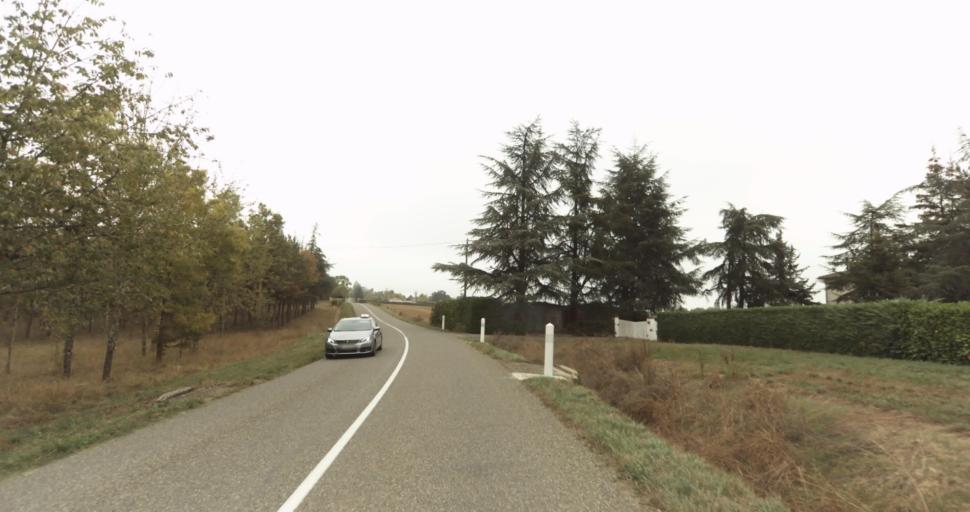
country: FR
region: Midi-Pyrenees
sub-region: Departement du Gers
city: Auch
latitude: 43.6330
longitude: 0.5251
